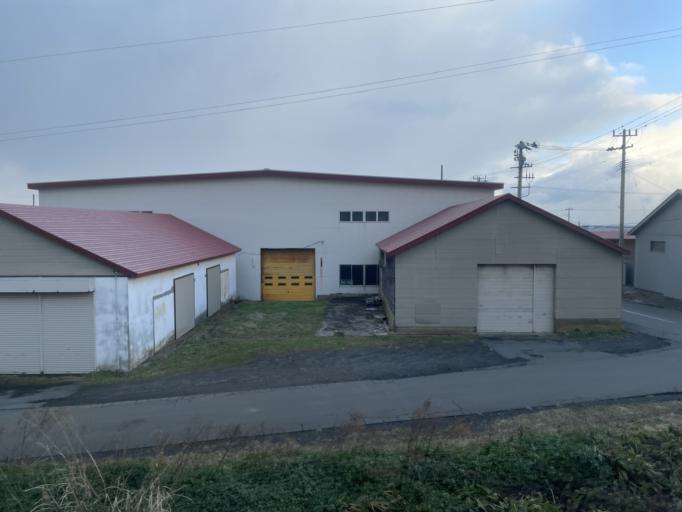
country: JP
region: Aomori
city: Mutsu
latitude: 41.0892
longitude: 141.2496
